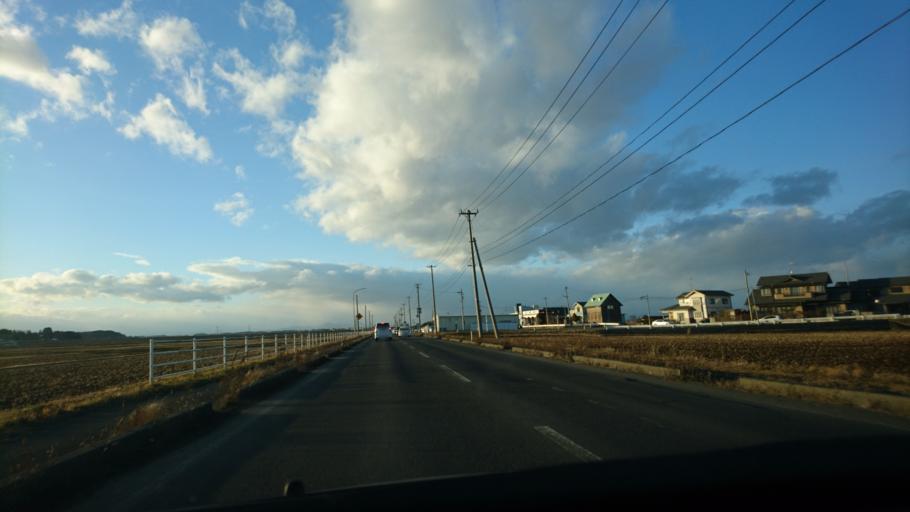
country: JP
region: Miyagi
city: Wakuya
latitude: 38.7153
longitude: 141.1669
